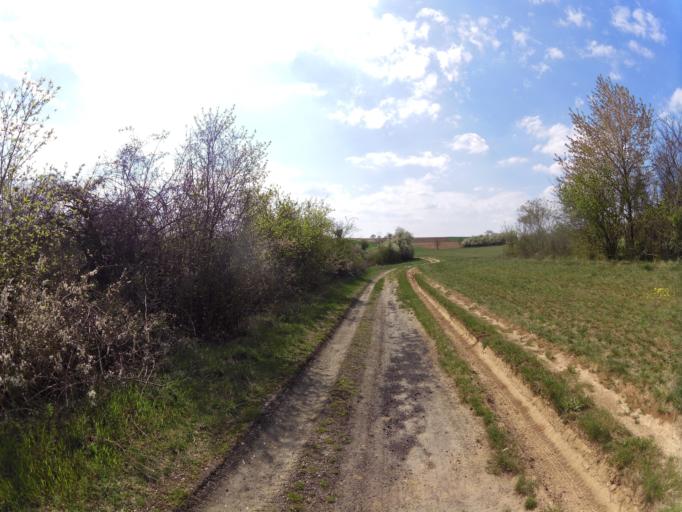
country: DE
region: Bavaria
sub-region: Regierungsbezirk Unterfranken
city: Winterhausen
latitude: 49.6874
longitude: 10.0121
